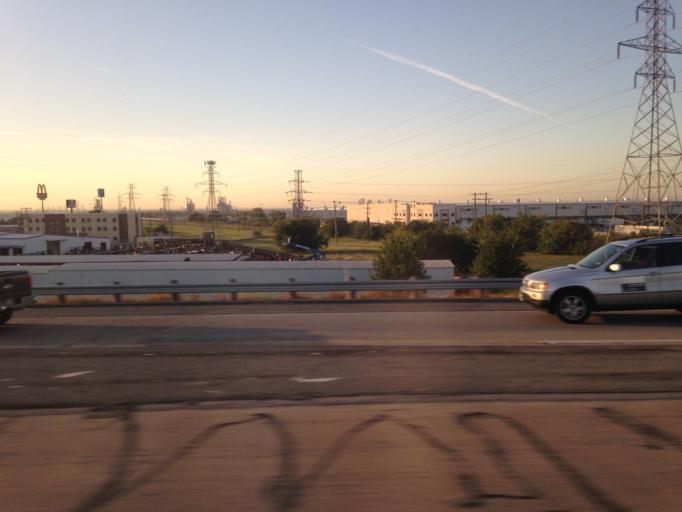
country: US
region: Texas
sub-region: Tarrant County
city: Blue Mound
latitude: 32.8426
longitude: -97.3464
